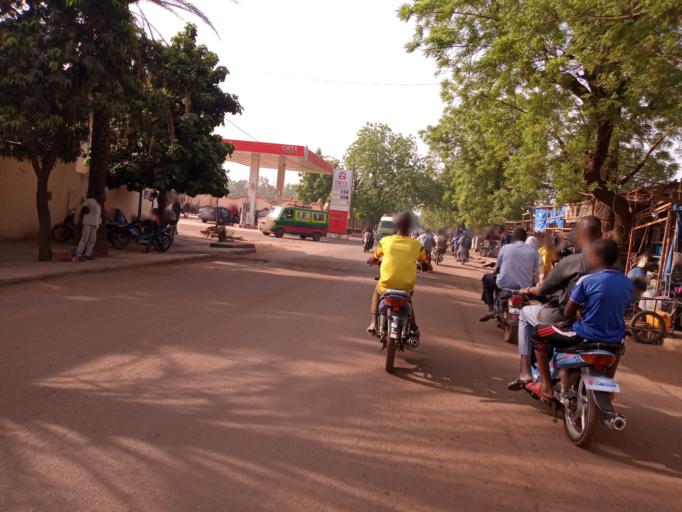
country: ML
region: Bamako
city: Bamako
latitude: 12.6591
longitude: -7.9809
